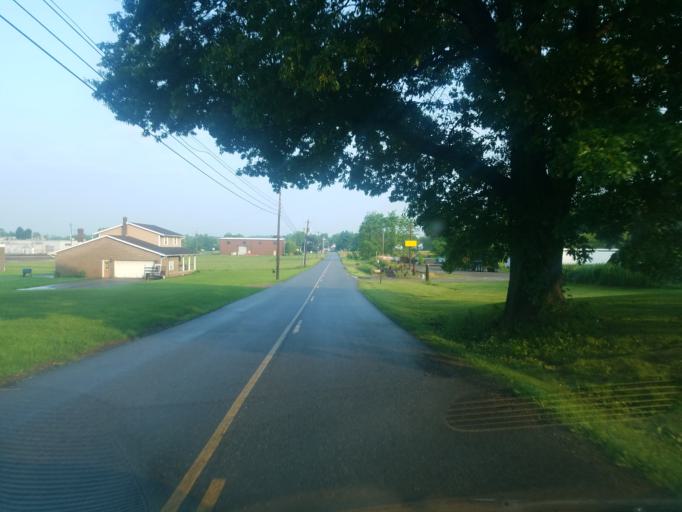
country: US
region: Ohio
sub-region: Stark County
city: Minerva
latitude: 40.7174
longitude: -81.0957
